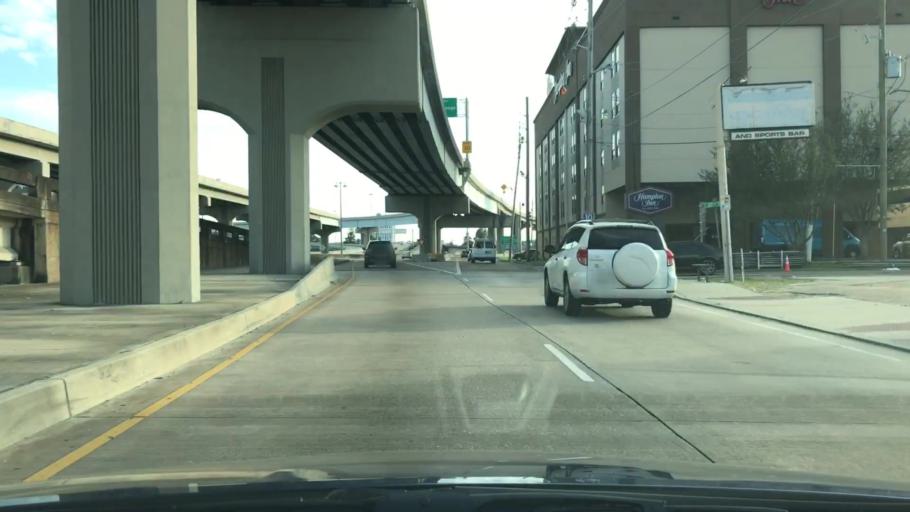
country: US
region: Louisiana
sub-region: Jefferson Parish
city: Metairie
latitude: 30.0024
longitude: -90.1555
